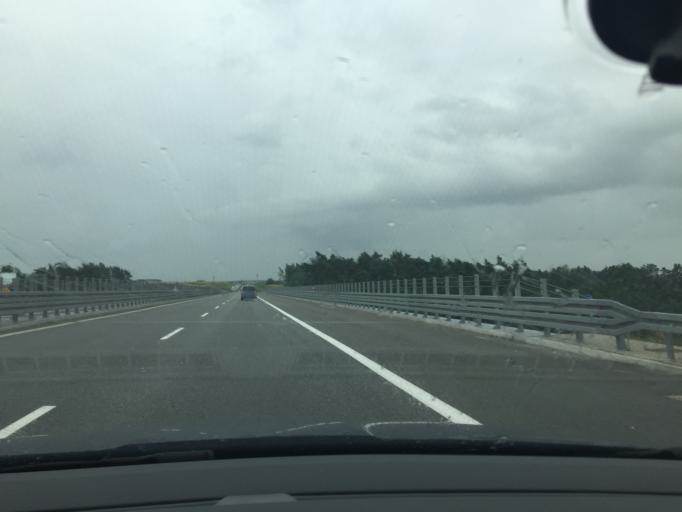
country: PL
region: Kujawsko-Pomorskie
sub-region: Powiat chelminski
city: Lisewo
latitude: 53.3626
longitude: 18.6988
